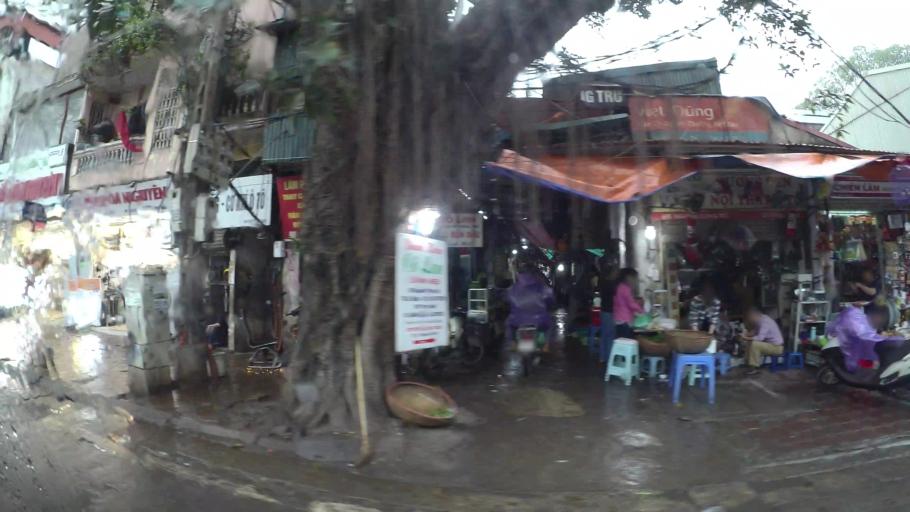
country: VN
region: Ha Noi
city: Hai BaTrung
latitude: 21.0138
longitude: 105.8541
